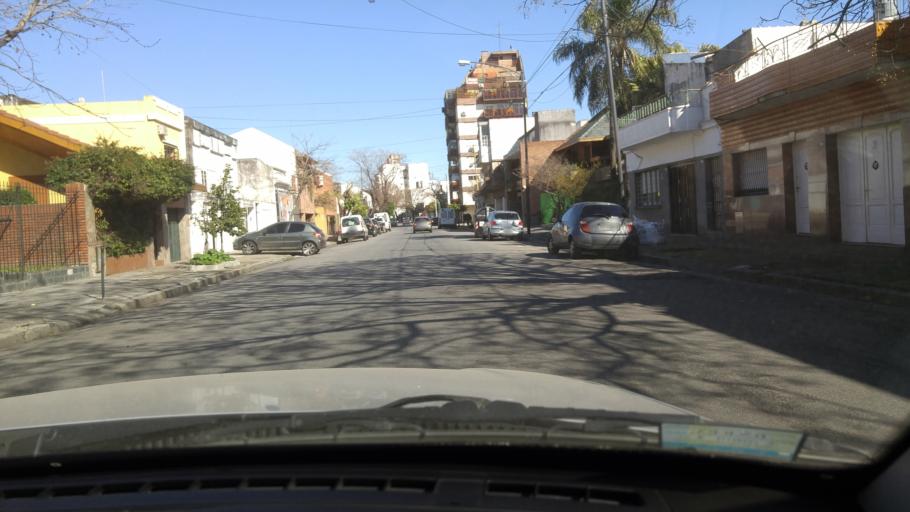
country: AR
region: Buenos Aires F.D.
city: Villa Santa Rita
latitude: -34.6196
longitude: -58.4807
